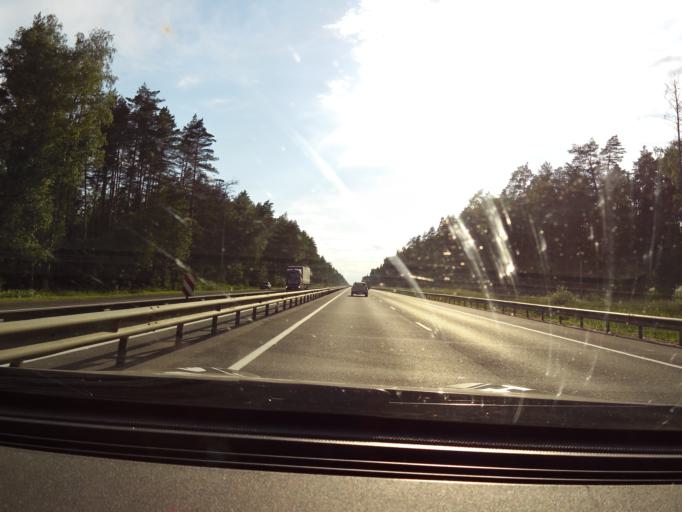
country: RU
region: Vladimir
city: Stepantsevo
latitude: 56.2219
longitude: 41.5384
